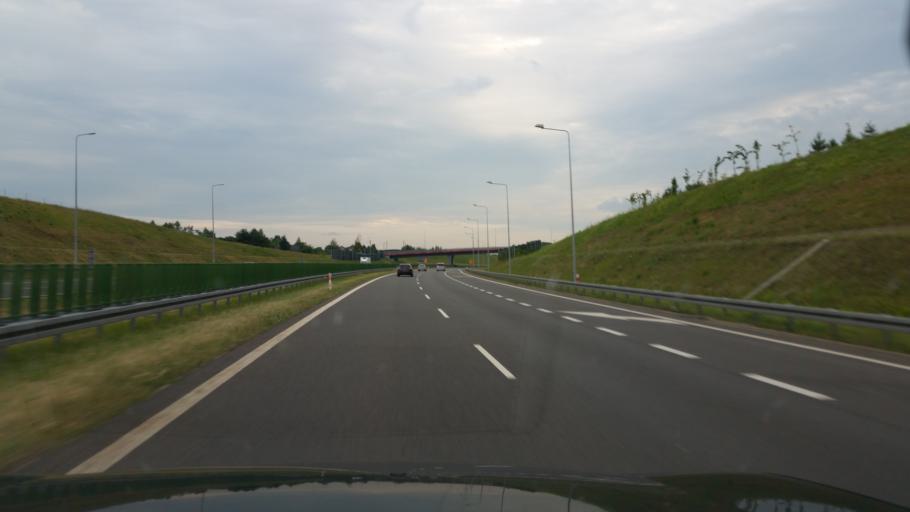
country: PL
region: Silesian Voivodeship
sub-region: Powiat rybnicki
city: Swierklany Gorne
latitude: 50.0226
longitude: 18.6007
